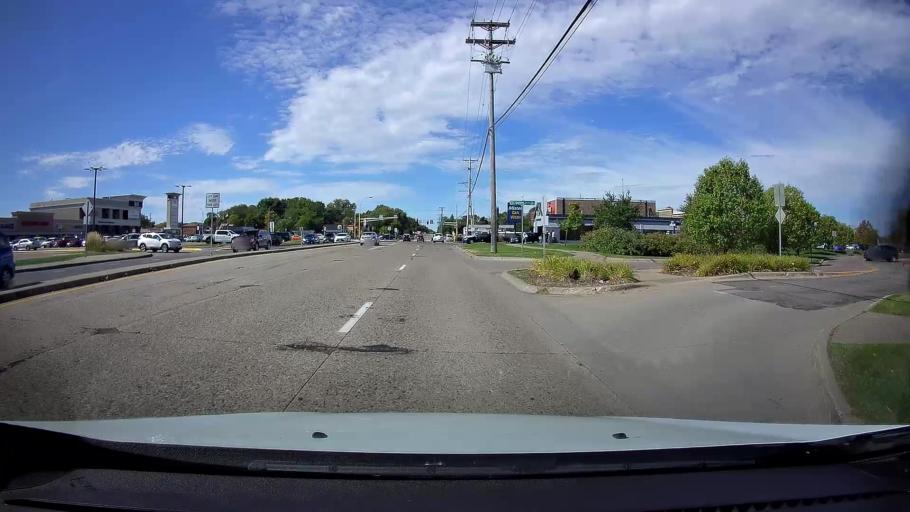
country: US
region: Minnesota
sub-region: Ramsey County
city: Roseville
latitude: 45.0063
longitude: -93.1644
